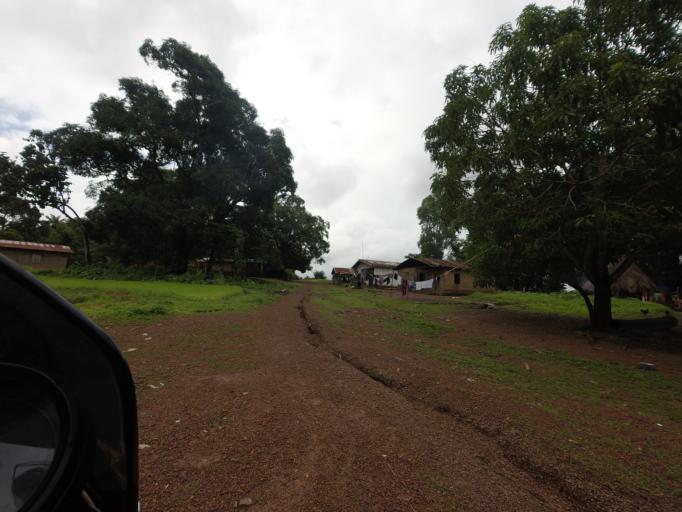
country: SL
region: Northern Province
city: Mambolo
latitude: 8.9708
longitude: -12.9996
